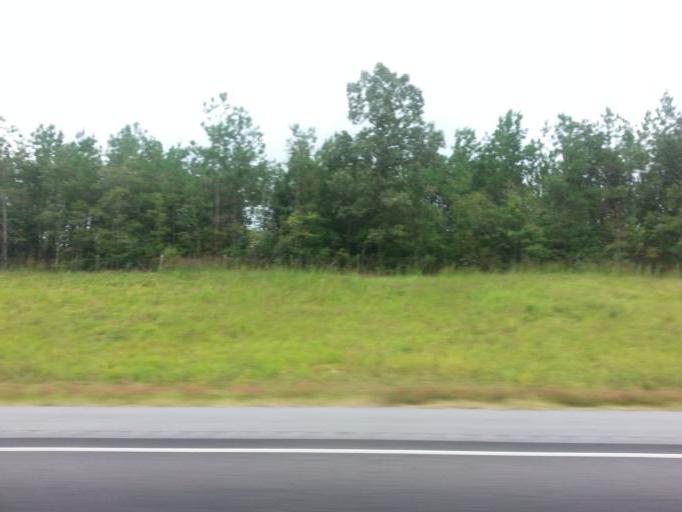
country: US
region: Alabama
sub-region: Conecuh County
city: Evergreen
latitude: 31.3476
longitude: -87.0901
